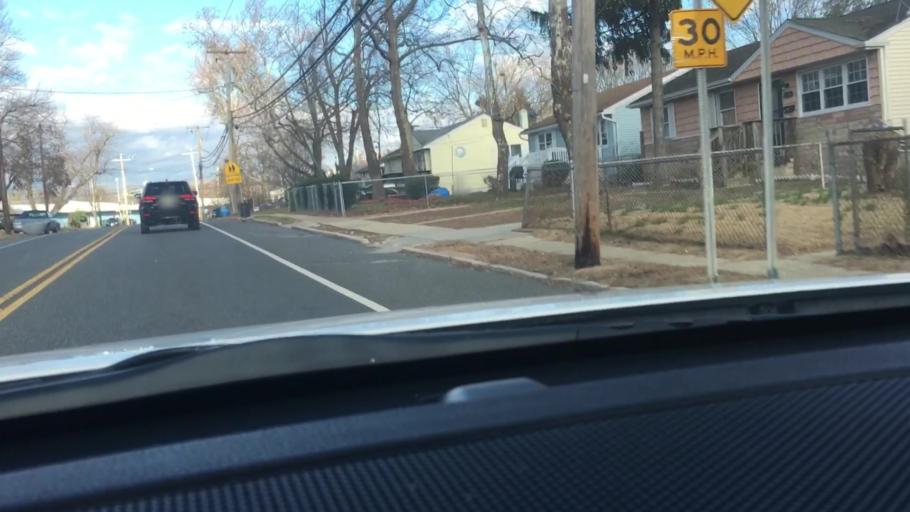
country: US
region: New Jersey
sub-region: Atlantic County
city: Pleasantville
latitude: 39.4105
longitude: -74.5184
